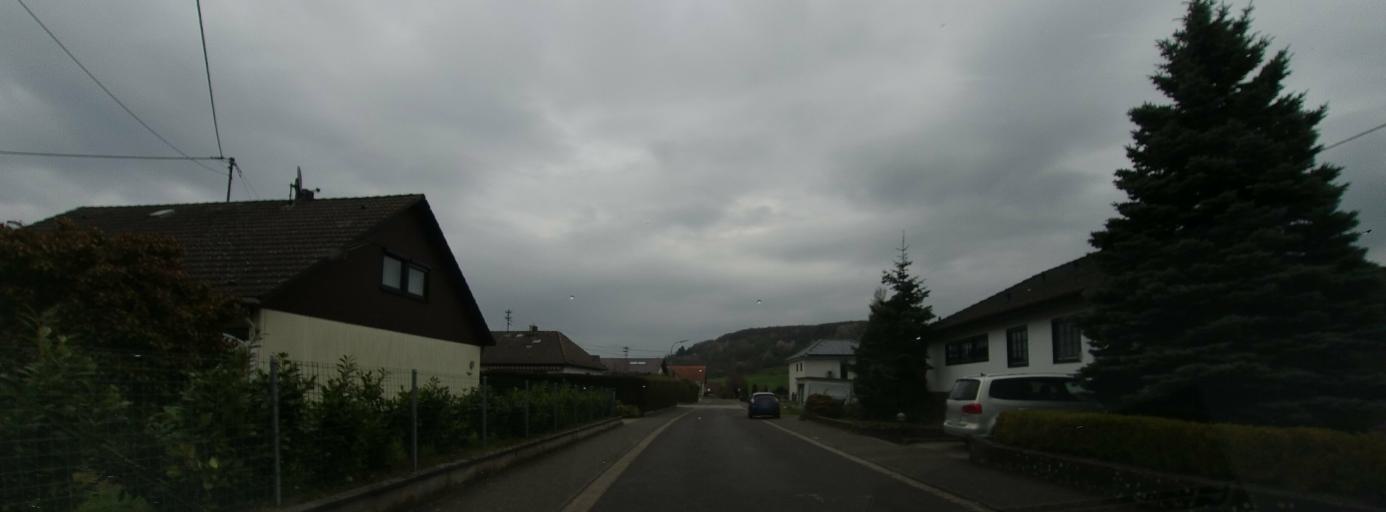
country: DE
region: Saarland
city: Losheim
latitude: 49.4991
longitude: 6.7738
